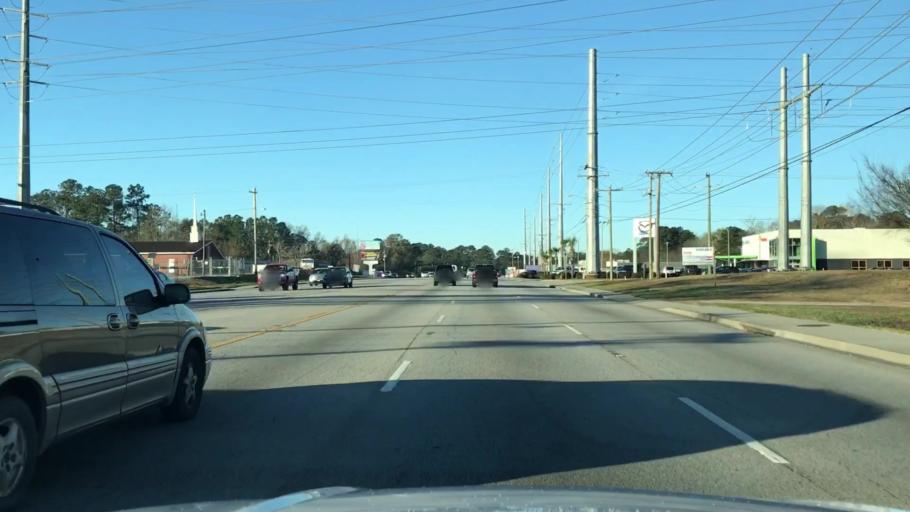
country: US
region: South Carolina
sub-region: Berkeley County
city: Hanahan
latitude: 32.9270
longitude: -80.0792
